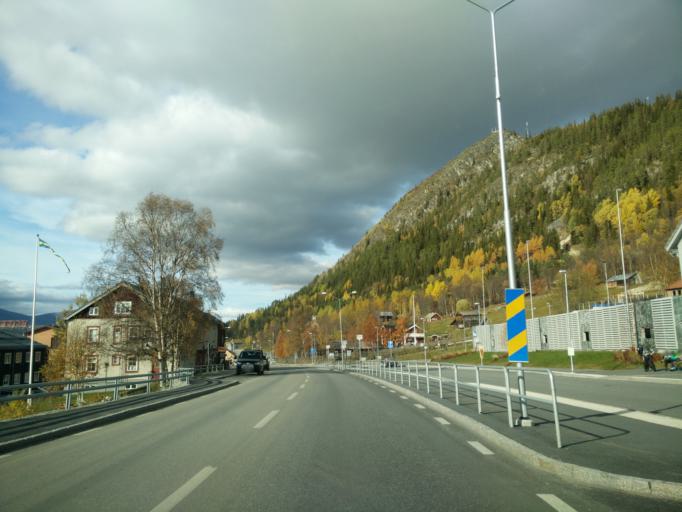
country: NO
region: Hedmark
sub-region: Engerdal
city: Engerdal
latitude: 62.5449
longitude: 12.5456
